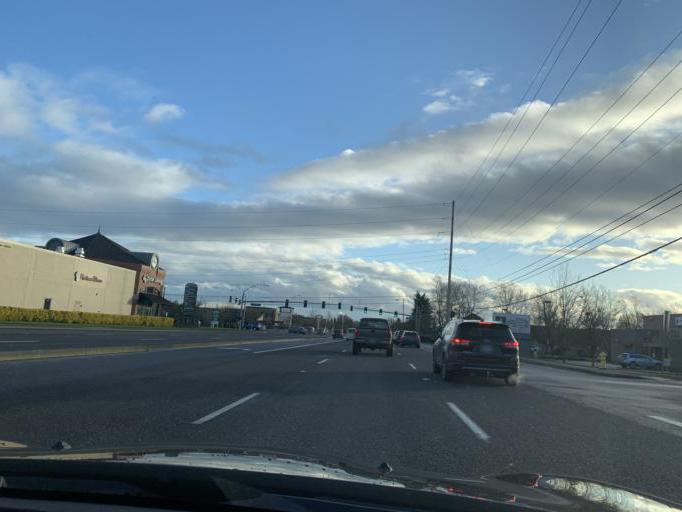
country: US
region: Washington
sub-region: Clark County
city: Mill Plain
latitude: 45.6112
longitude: -122.5043
